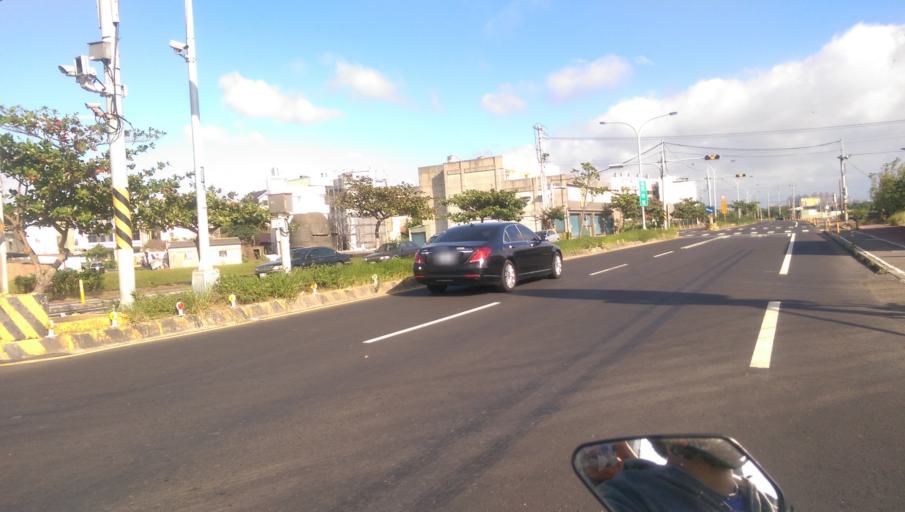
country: TW
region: Taiwan
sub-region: Hsinchu
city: Hsinchu
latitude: 24.8349
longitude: 120.9422
